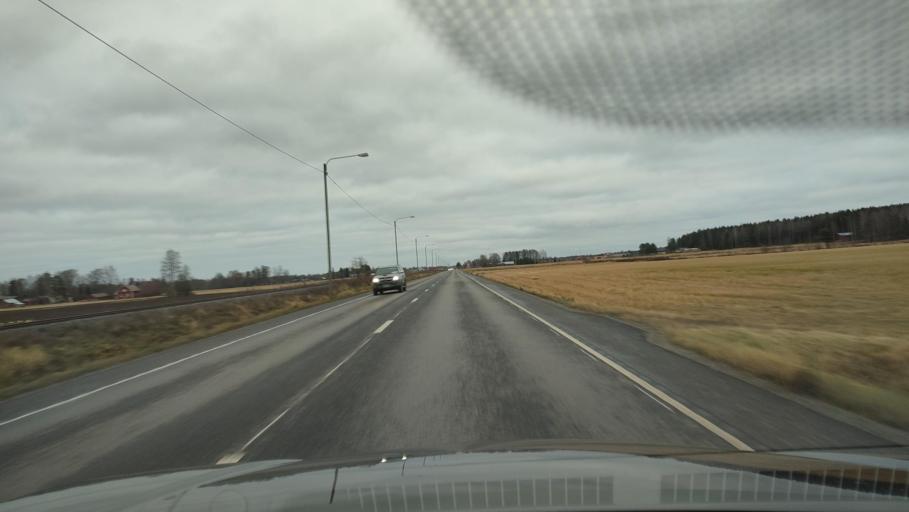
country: FI
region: Southern Ostrobothnia
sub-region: Seinaejoki
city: Ilmajoki
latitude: 62.7086
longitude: 22.5332
